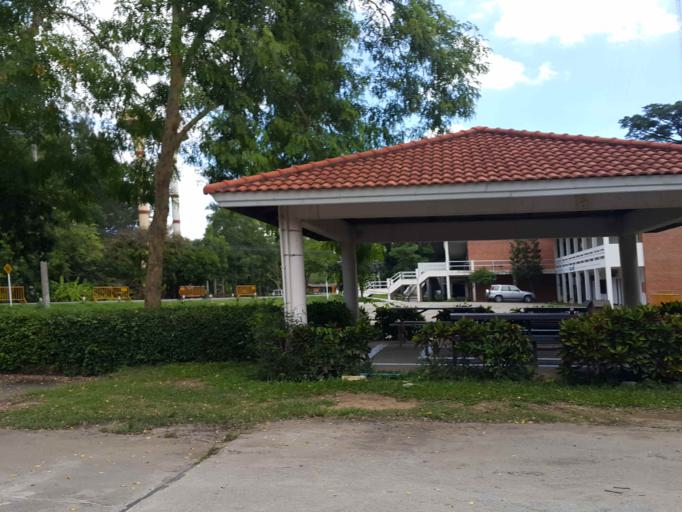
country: TH
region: Chiang Mai
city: Chiang Mai
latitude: 18.7941
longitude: 99.0313
